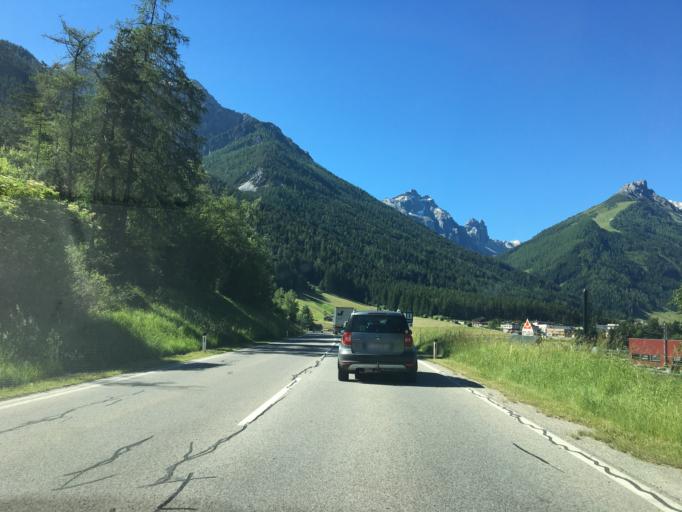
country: AT
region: Tyrol
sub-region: Politischer Bezirk Innsbruck Land
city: Neustift im Stubaital
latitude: 47.1357
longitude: 11.3406
